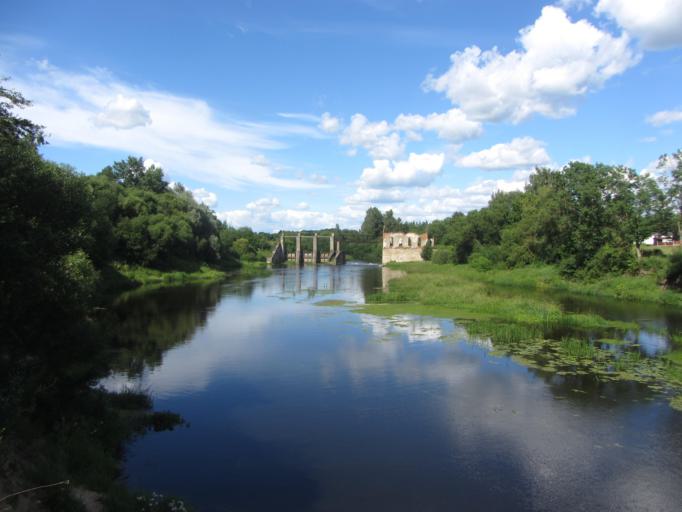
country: LT
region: Kauno apskritis
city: Kedainiai
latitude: 55.3650
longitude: 24.0114
